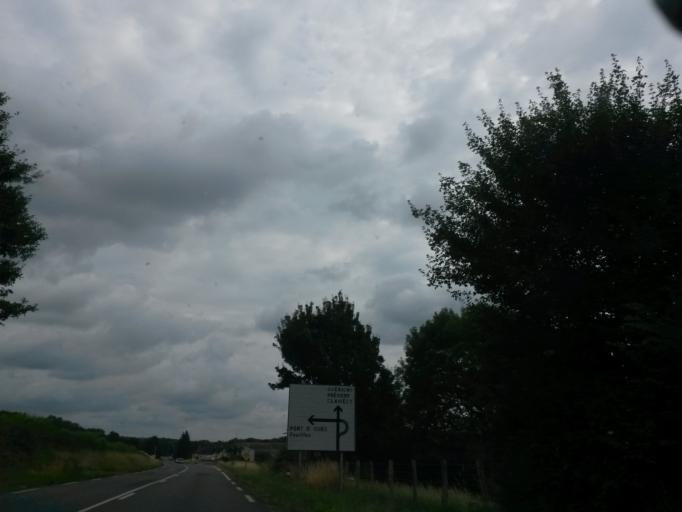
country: FR
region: Bourgogne
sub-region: Departement de la Nievre
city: Coulanges-les-Nevers
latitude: 47.0172
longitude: 3.2071
